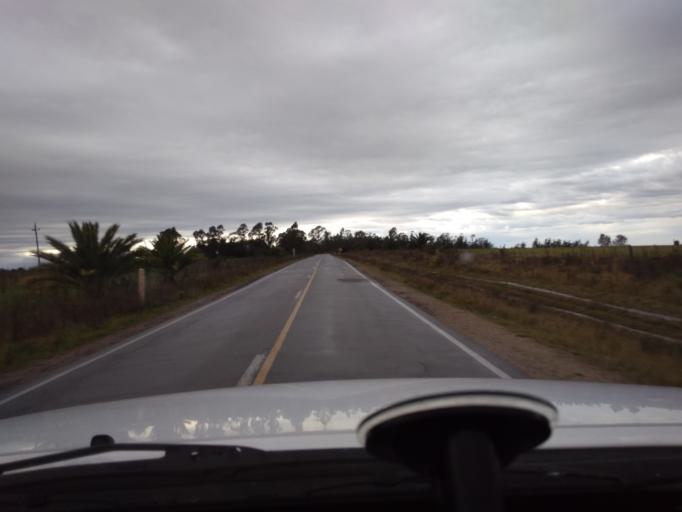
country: UY
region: Canelones
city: San Ramon
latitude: -34.3014
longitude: -55.9348
